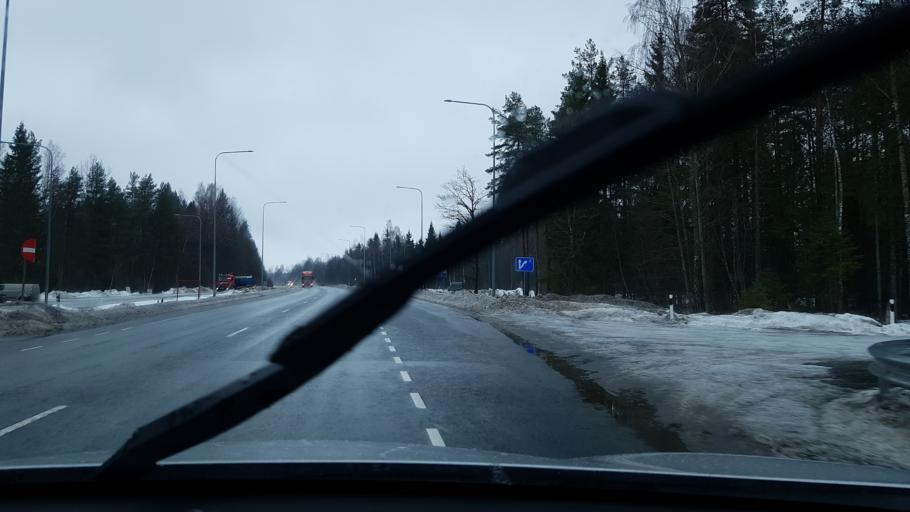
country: EE
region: Raplamaa
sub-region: Kohila vald
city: Kohila
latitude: 59.1288
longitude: 24.7910
